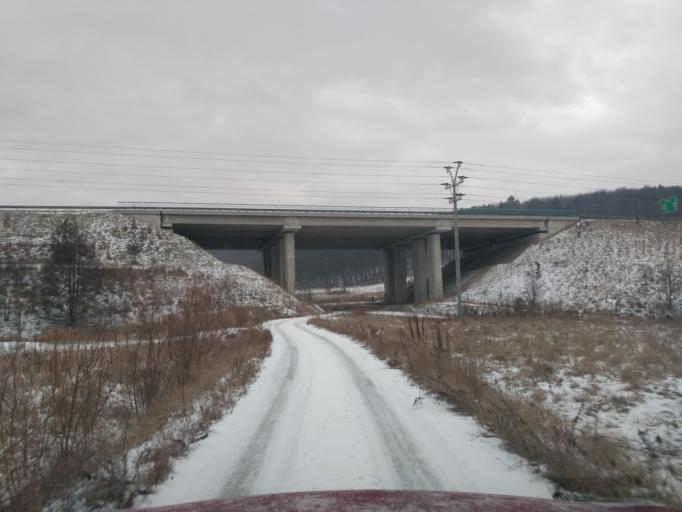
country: SK
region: Presovsky
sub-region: Okres Presov
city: Presov
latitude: 49.0037
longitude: 21.1761
